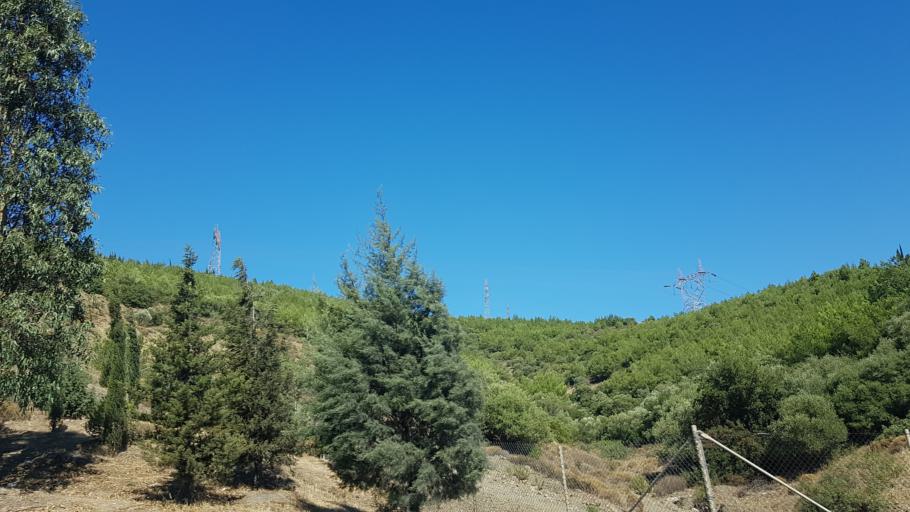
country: TR
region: Izmir
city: Buca
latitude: 38.4066
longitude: 27.2336
